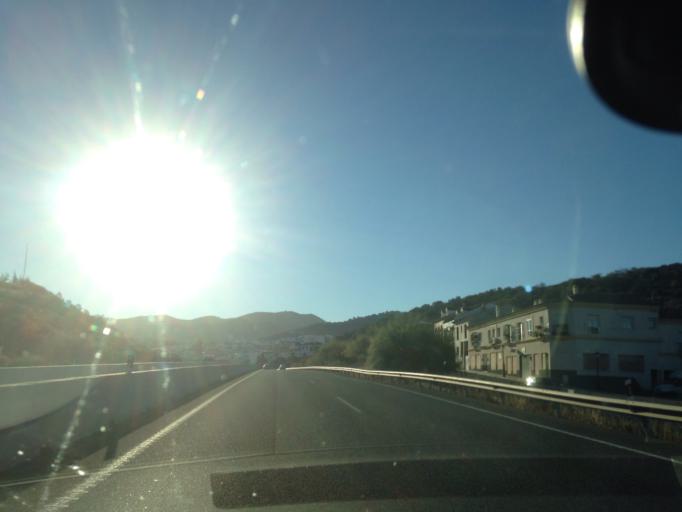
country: ES
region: Andalusia
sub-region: Provincia de Malaga
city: Casabermeja
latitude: 36.8996
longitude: -4.4370
